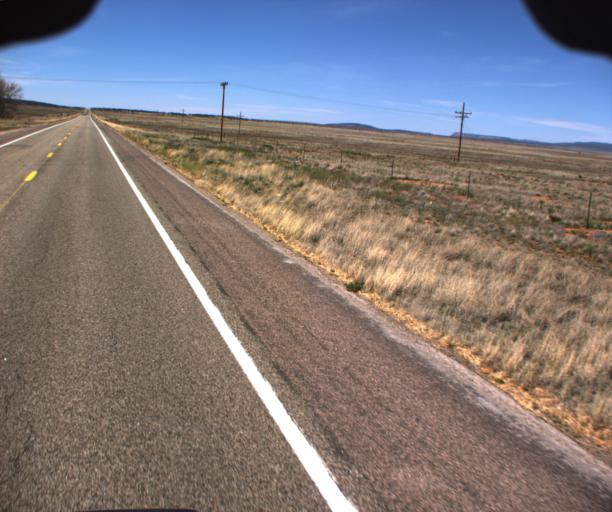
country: US
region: Arizona
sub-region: Mohave County
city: Peach Springs
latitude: 35.4777
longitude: -113.1366
